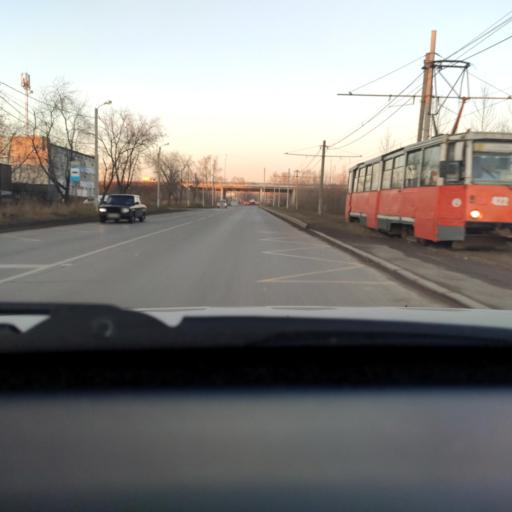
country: RU
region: Perm
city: Kondratovo
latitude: 57.9431
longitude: 56.1260
